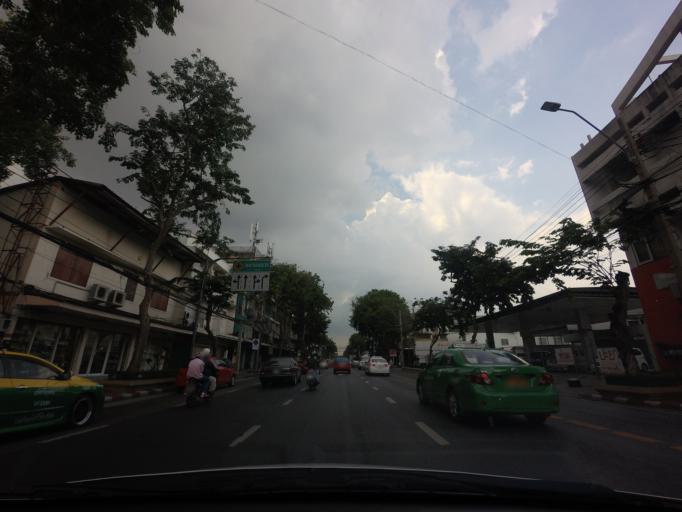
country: TH
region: Bangkok
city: Pom Prap Sattru Phai
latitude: 13.7565
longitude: 100.5108
